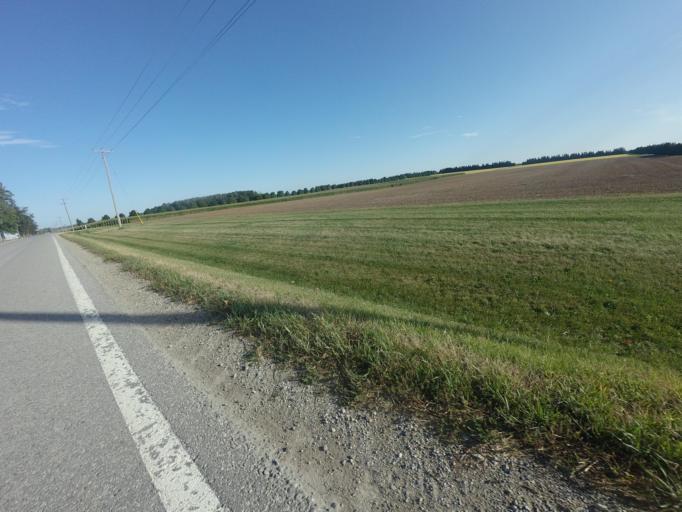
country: CA
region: Ontario
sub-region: Wellington County
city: Guelph
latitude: 43.6413
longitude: -80.4028
